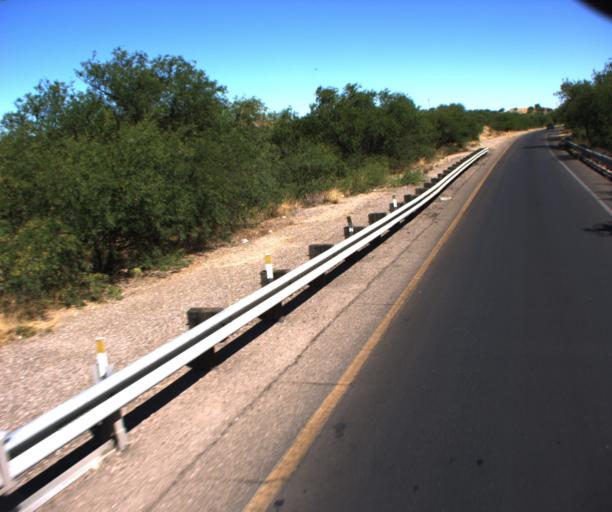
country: US
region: Arizona
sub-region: Santa Cruz County
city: Nogales
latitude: 31.3966
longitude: -110.9585
